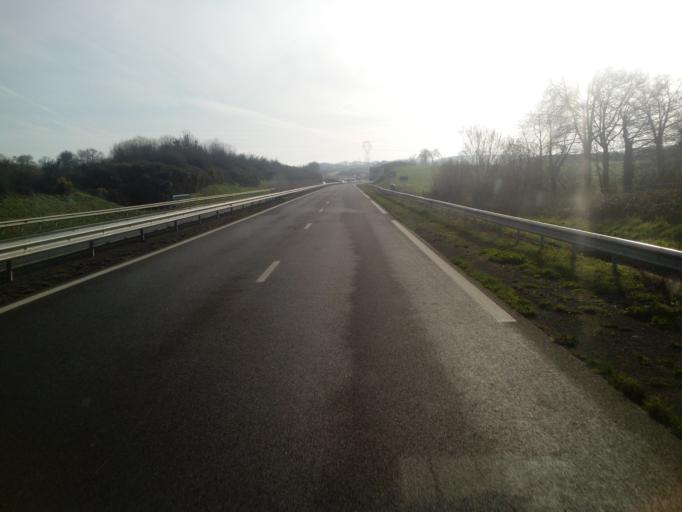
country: FR
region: Brittany
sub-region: Departement d'Ille-et-Vilaine
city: Betton
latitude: 48.1595
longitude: -1.6258
